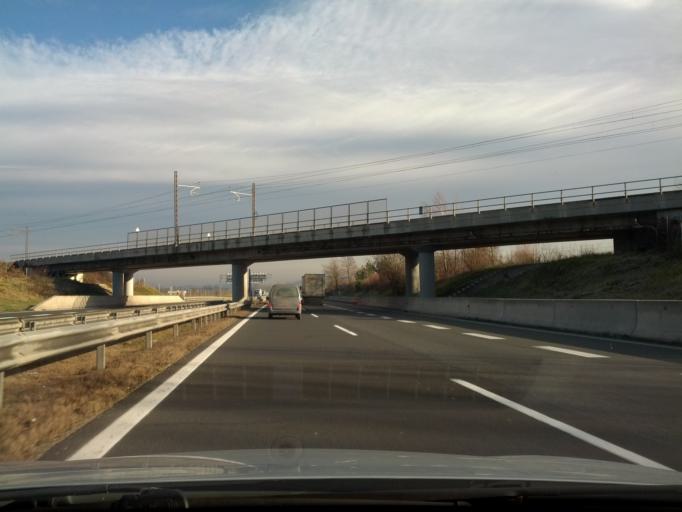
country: SI
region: Hoce-Slivnica
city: Radizel
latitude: 46.4877
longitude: 15.6623
